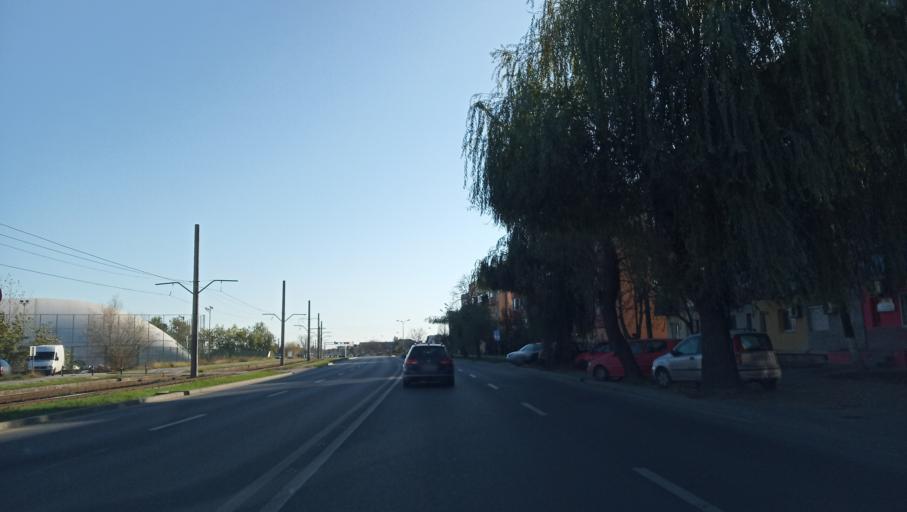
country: RO
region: Timis
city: Timisoara
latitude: 45.7311
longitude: 21.2628
